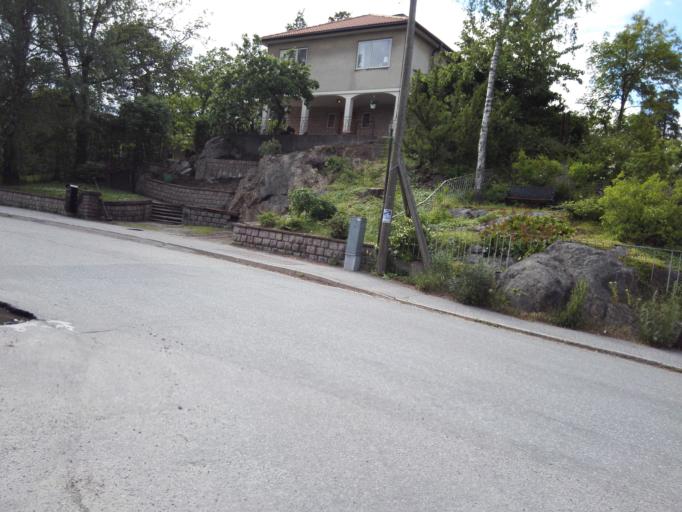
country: SE
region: Stockholm
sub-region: Huddinge Kommun
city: Huddinge
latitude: 59.2530
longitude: 18.0005
